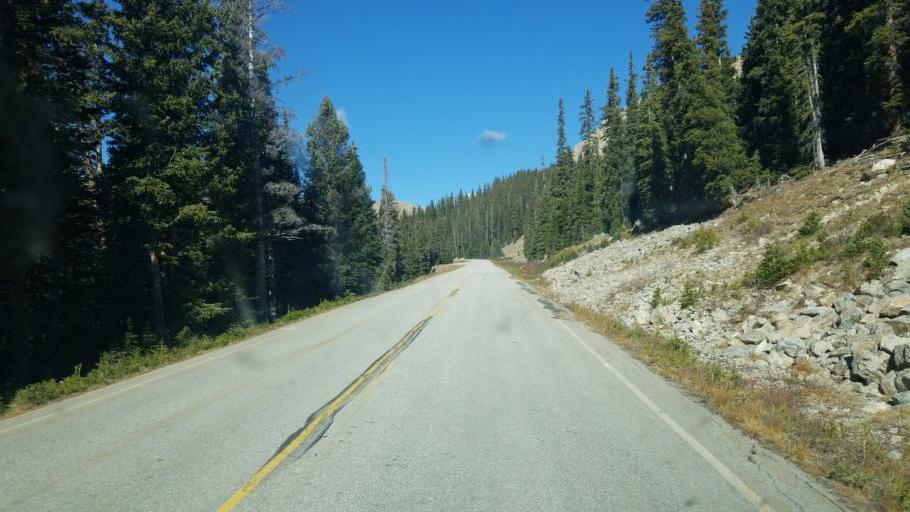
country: US
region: Colorado
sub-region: Chaffee County
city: Buena Vista
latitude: 38.8125
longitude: -106.3949
